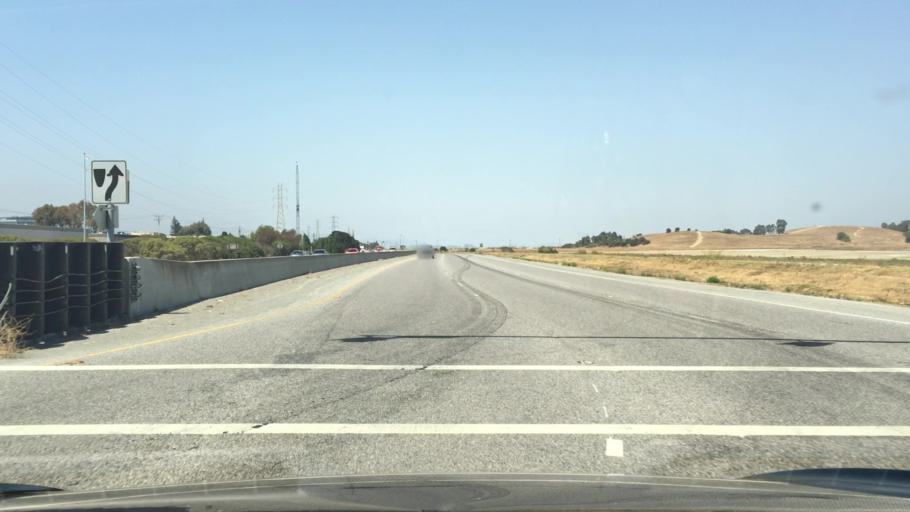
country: US
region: California
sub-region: San Mateo County
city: East Palo Alto
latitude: 37.4833
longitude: -122.1673
